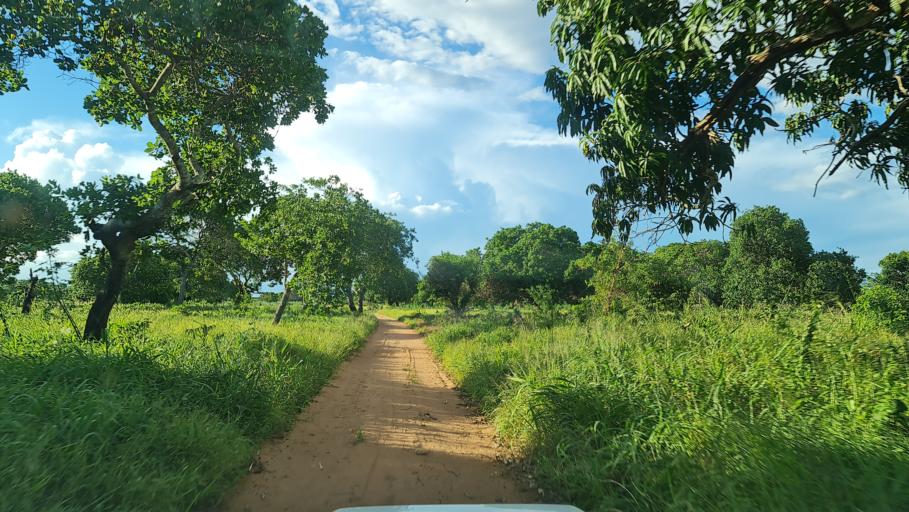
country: MZ
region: Nampula
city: Ilha de Mocambique
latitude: -14.9493
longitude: 40.1694
